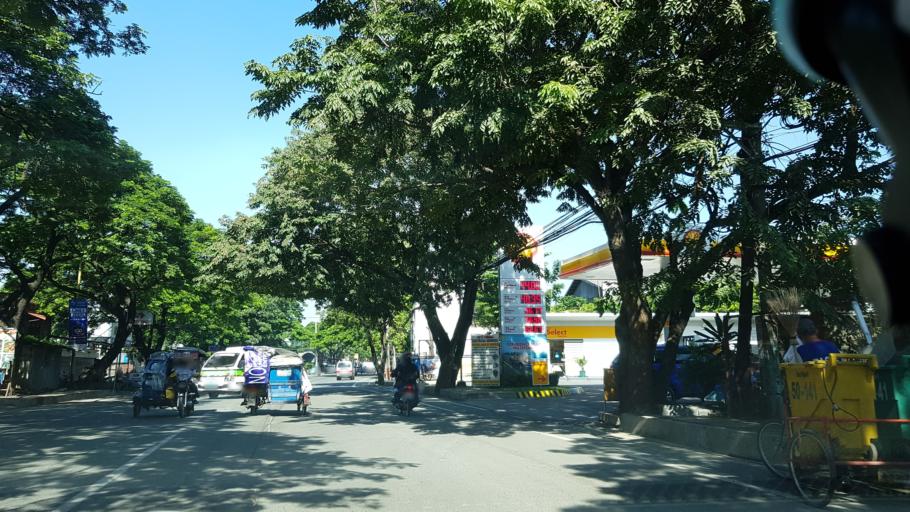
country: PH
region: Calabarzon
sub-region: Province of Rizal
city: Pateros
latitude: 14.5676
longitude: 121.0892
